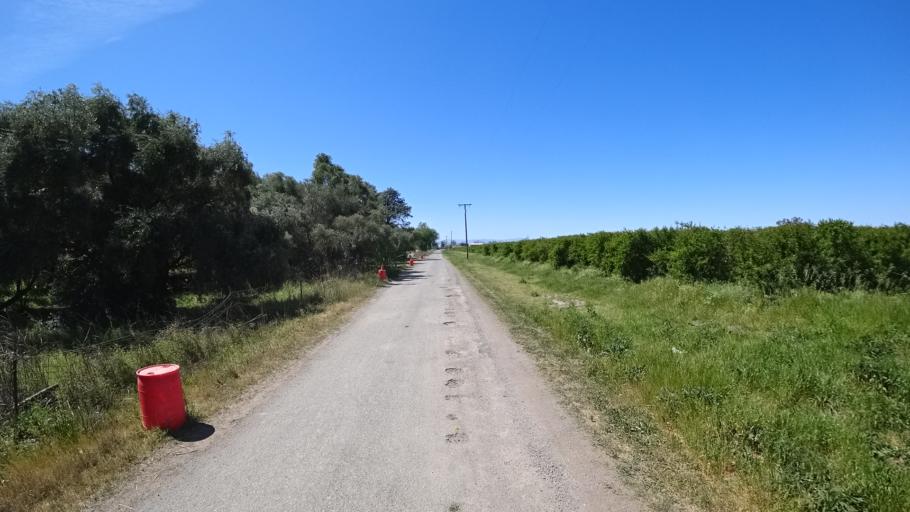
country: US
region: California
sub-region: Glenn County
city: Hamilton City
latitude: 39.7287
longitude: -122.0890
